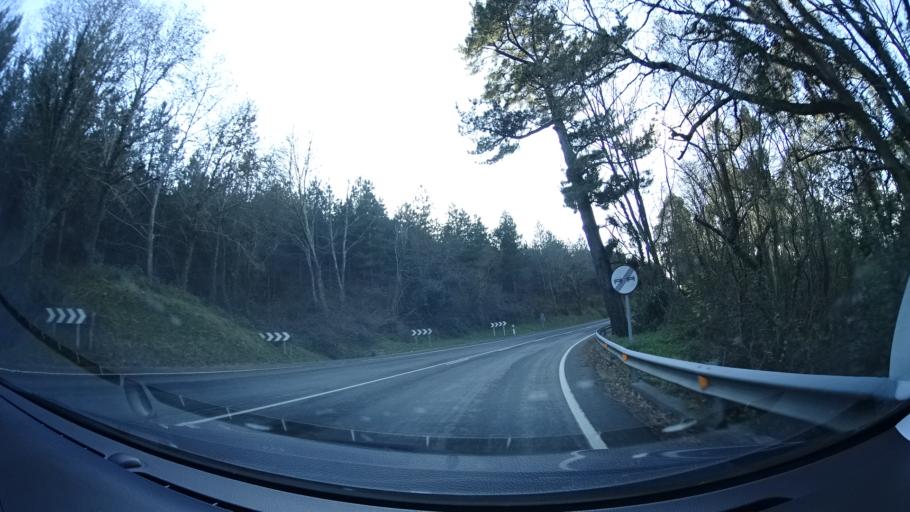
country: ES
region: Basque Country
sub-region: Bizkaia
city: Bermeo
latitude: 43.3979
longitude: -2.7600
